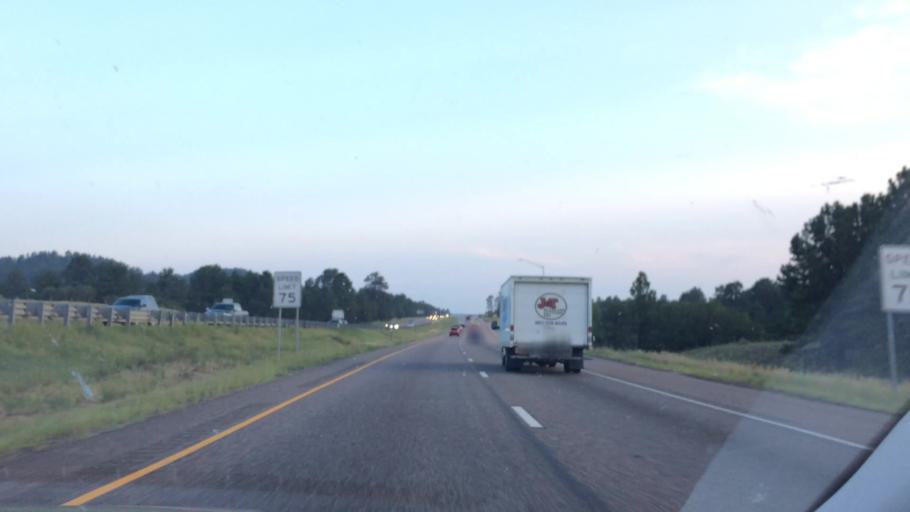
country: US
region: Colorado
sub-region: Douglas County
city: Perry Park
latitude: 39.2338
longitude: -104.8775
